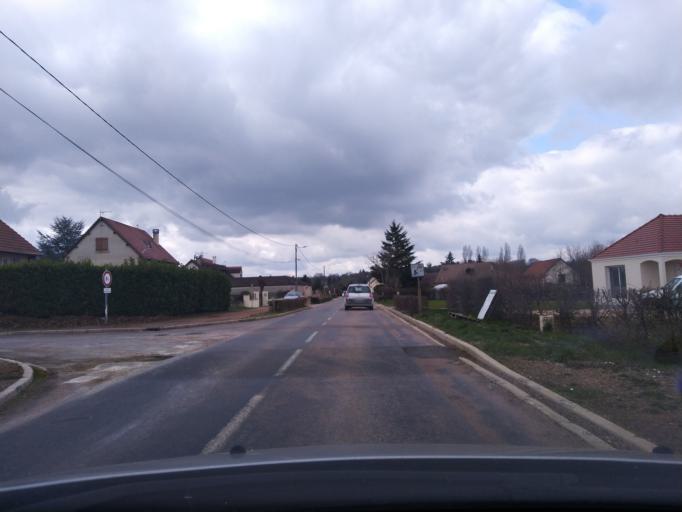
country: FR
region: Bourgogne
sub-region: Departement de l'Yonne
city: Avallon
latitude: 47.5188
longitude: 3.9521
